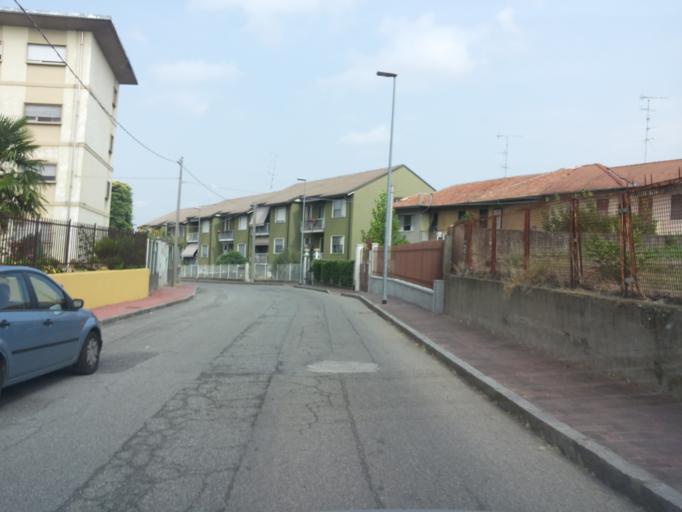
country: IT
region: Piedmont
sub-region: Provincia di Vercelli
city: Vercelli
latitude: 45.3090
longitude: 8.4441
